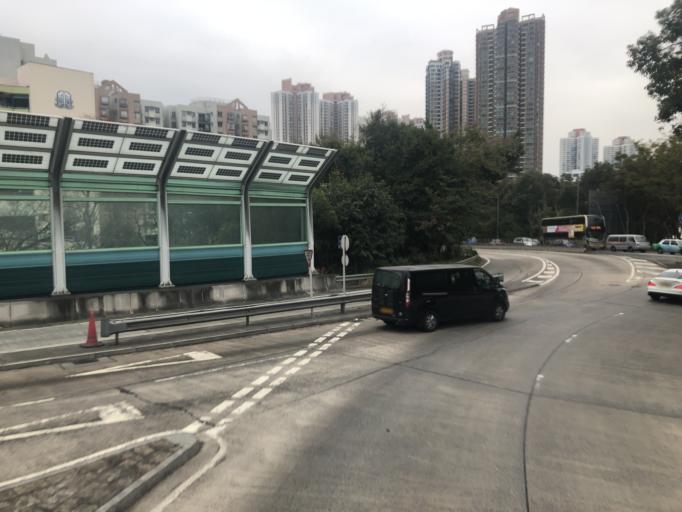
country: HK
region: Tai Po
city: Tai Po
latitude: 22.4972
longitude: 114.1314
